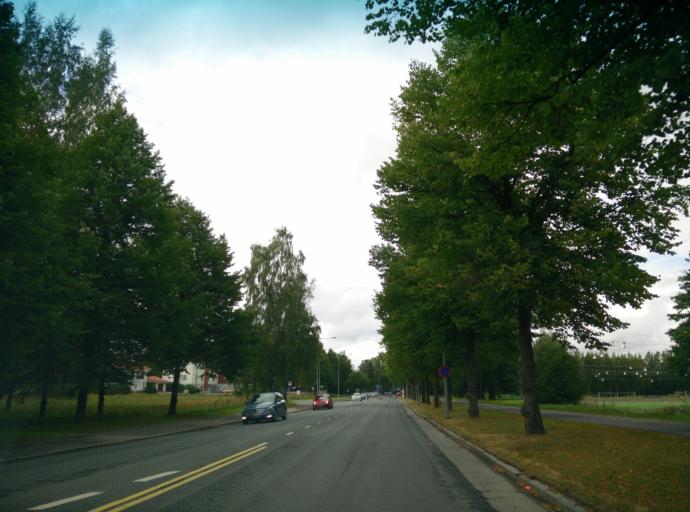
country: FI
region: Haeme
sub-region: Haemeenlinna
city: Haemeenlinna
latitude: 61.0013
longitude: 24.4286
